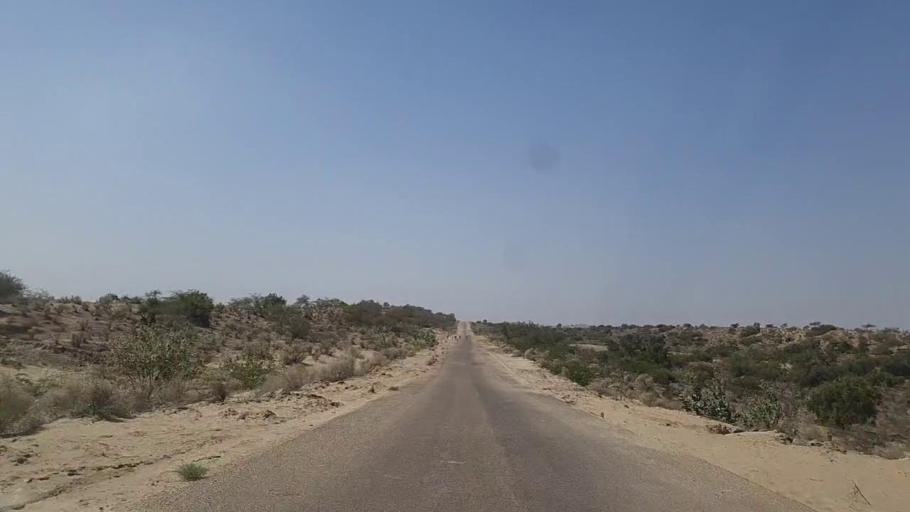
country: PK
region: Sindh
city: Diplo
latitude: 24.5529
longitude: 69.4334
